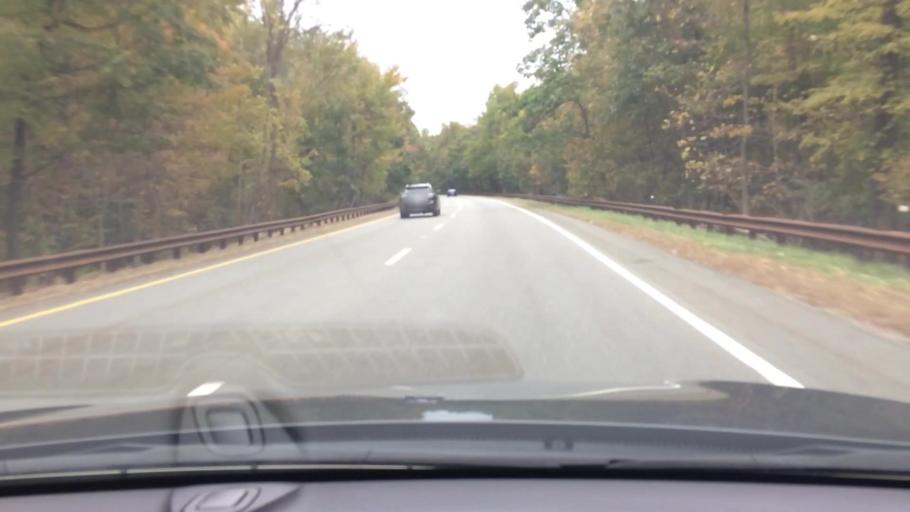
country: US
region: New Jersey
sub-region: Bergen County
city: Alpine
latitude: 40.9672
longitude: -73.9147
